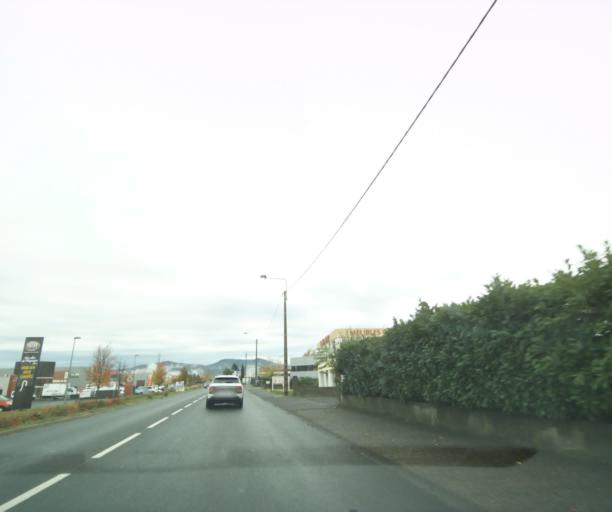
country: FR
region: Auvergne
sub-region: Departement du Puy-de-Dome
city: Le Cendre
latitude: 45.7338
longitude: 3.1797
